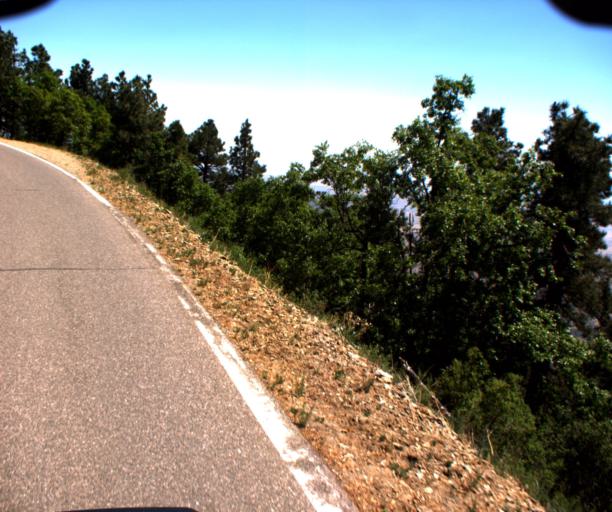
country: US
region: Arizona
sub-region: Graham County
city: Swift Trail Junction
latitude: 32.6356
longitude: -109.8485
